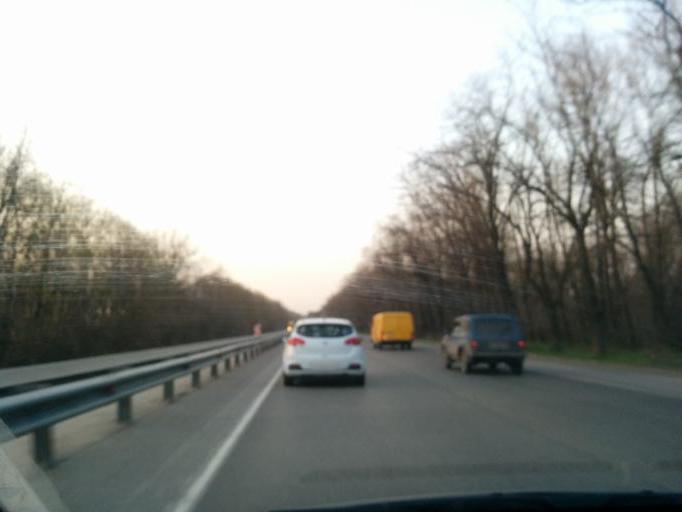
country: RU
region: Rostov
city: Aksay
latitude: 47.3108
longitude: 39.8633
